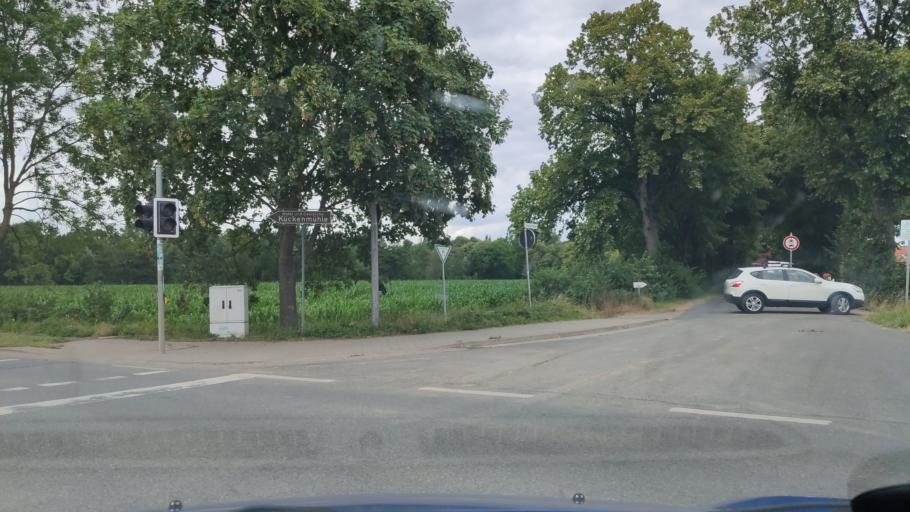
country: DE
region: Lower Saxony
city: Ronnenberg
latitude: 52.3095
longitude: 9.6799
